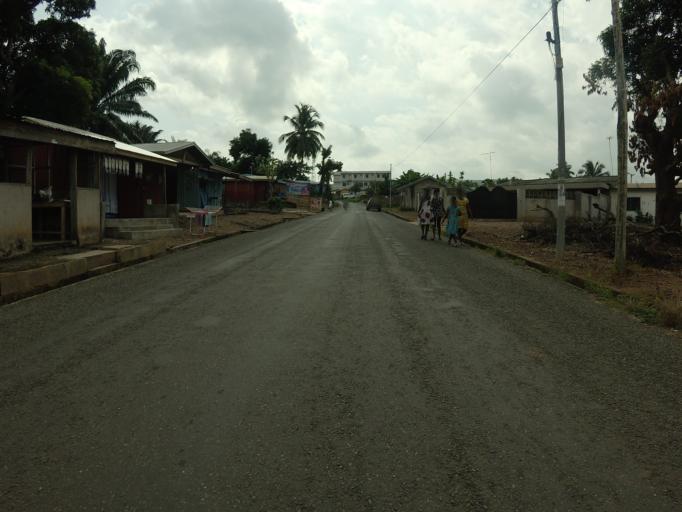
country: GH
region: Volta
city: Ho
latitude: 6.6176
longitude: 0.4759
